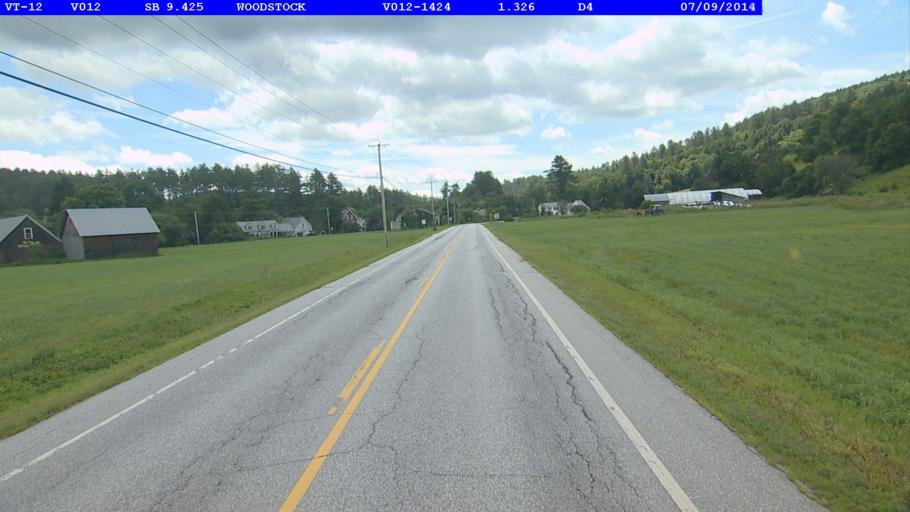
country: US
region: Vermont
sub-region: Windsor County
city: Woodstock
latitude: 43.6404
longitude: -72.5273
